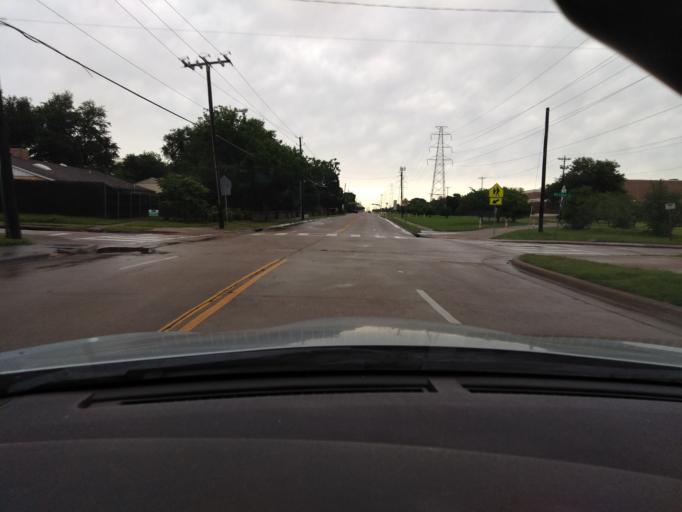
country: US
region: Texas
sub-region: Dallas County
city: Richardson
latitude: 32.9594
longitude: -96.7786
